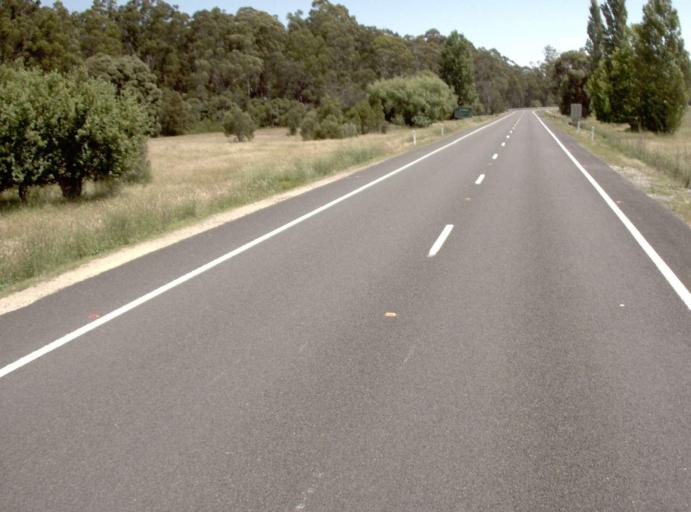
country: AU
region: New South Wales
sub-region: Bombala
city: Bombala
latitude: -37.5678
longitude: 149.1417
